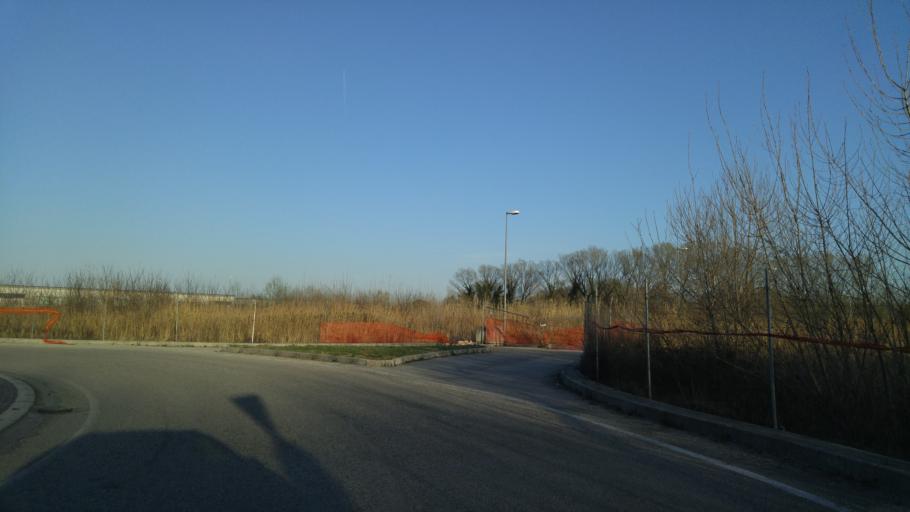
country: IT
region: The Marches
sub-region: Provincia di Pesaro e Urbino
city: Villa Ceccolini
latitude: 43.8947
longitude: 12.8390
